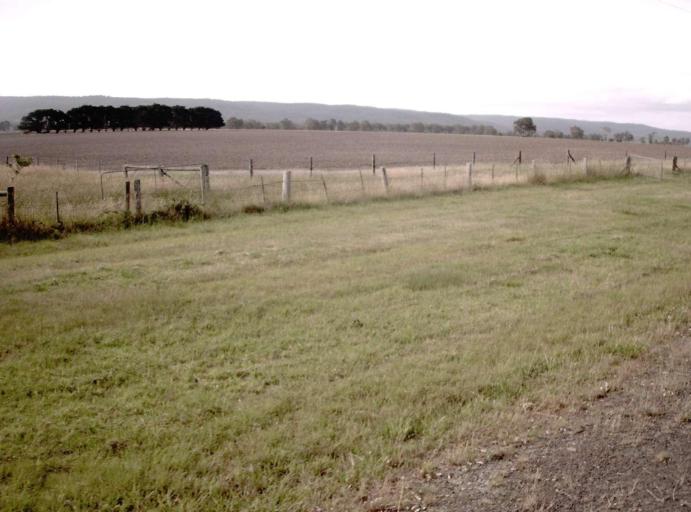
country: AU
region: Victoria
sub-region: Wellington
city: Heyfield
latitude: -38.0478
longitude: 146.6644
